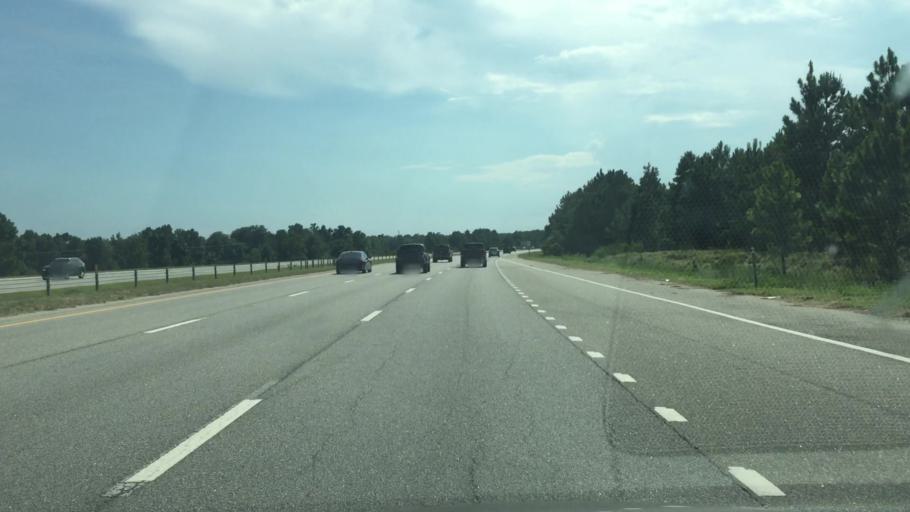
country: US
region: South Carolina
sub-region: Horry County
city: North Myrtle Beach
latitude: 33.8397
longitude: -78.7051
